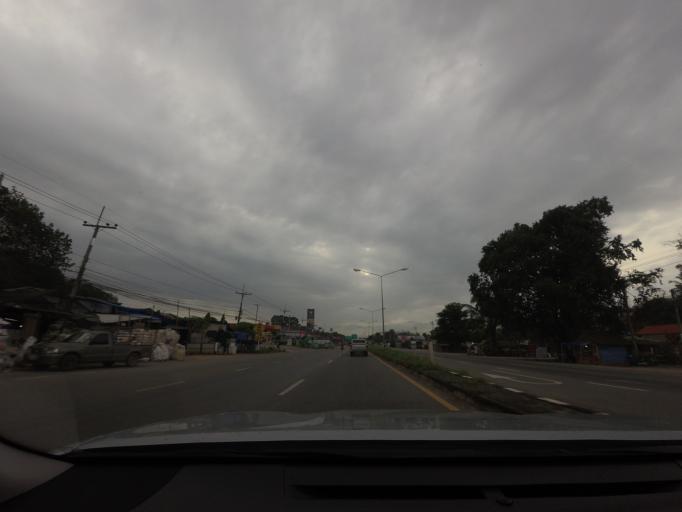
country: TH
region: Surat Thani
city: Phunphin
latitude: 9.0516
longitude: 99.1664
